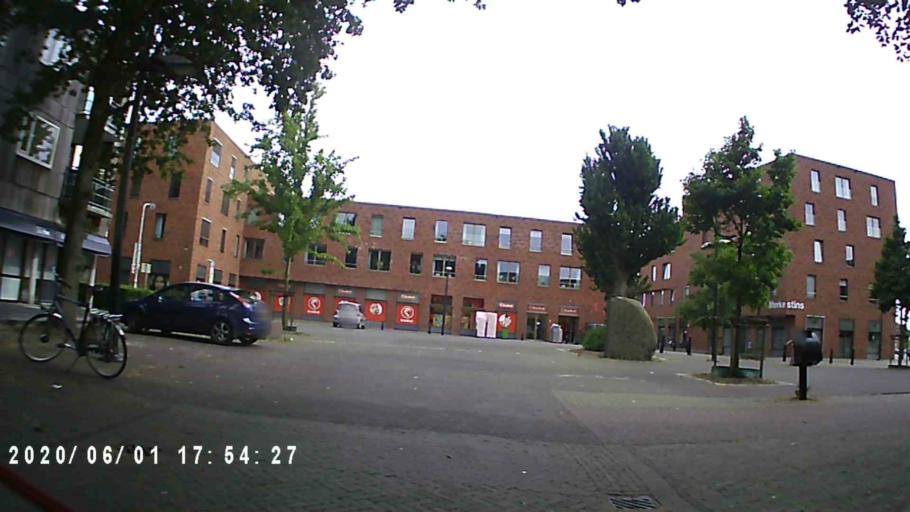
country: NL
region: Friesland
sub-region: Gemeente Tytsjerksteradiel
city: Burgum
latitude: 53.1922
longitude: 5.9941
